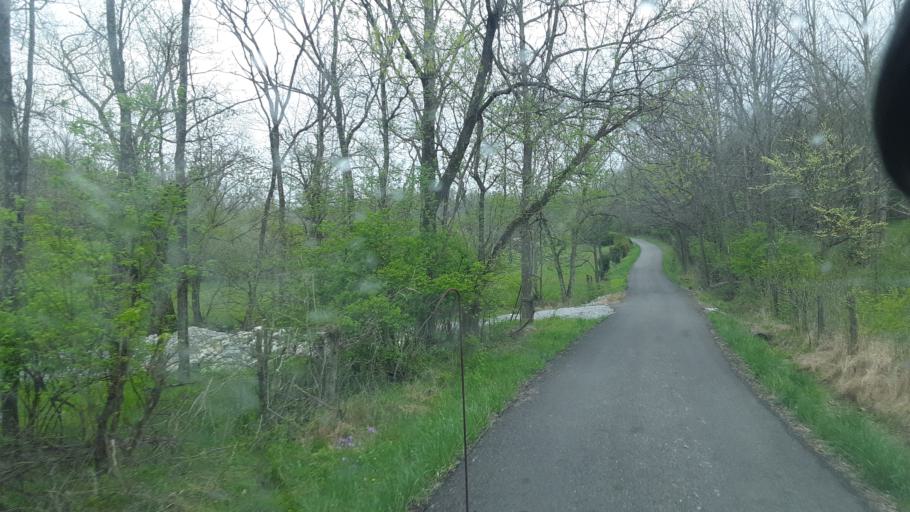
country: US
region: Kentucky
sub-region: Owen County
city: Owenton
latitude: 38.6715
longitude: -84.7948
